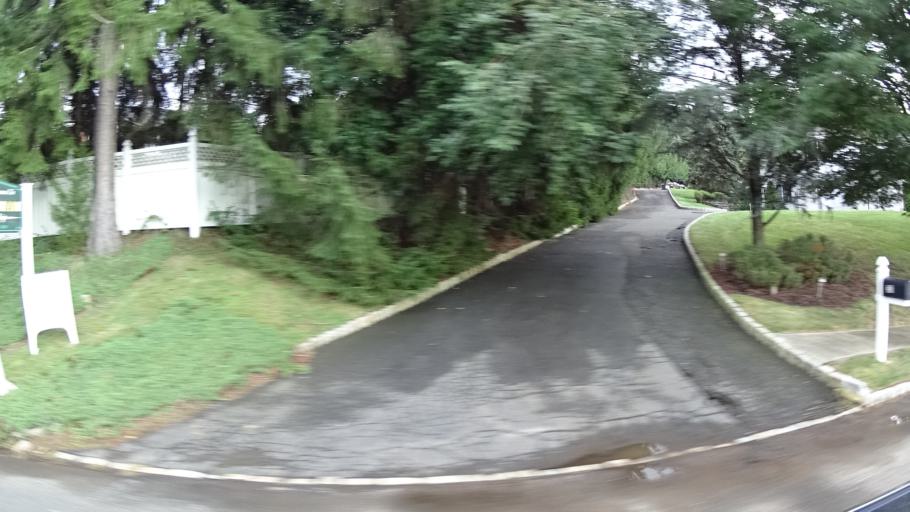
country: US
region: New Jersey
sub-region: Union County
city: Berkeley Heights
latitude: 40.6988
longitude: -74.4459
